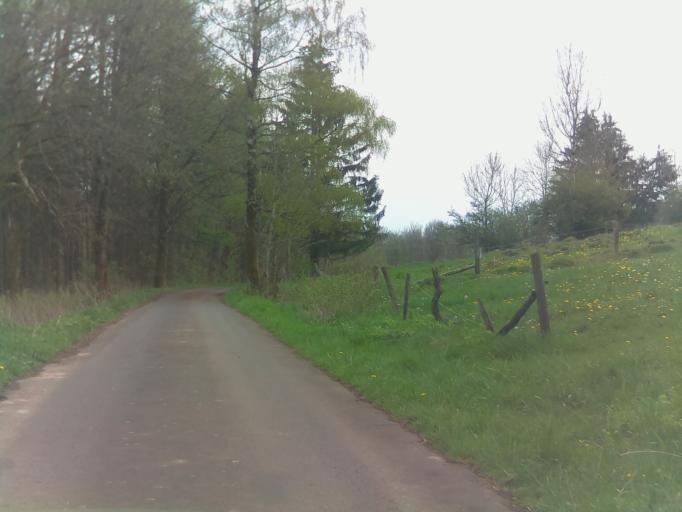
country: DE
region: Thuringia
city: Unterweid
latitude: 50.6309
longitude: 10.0707
